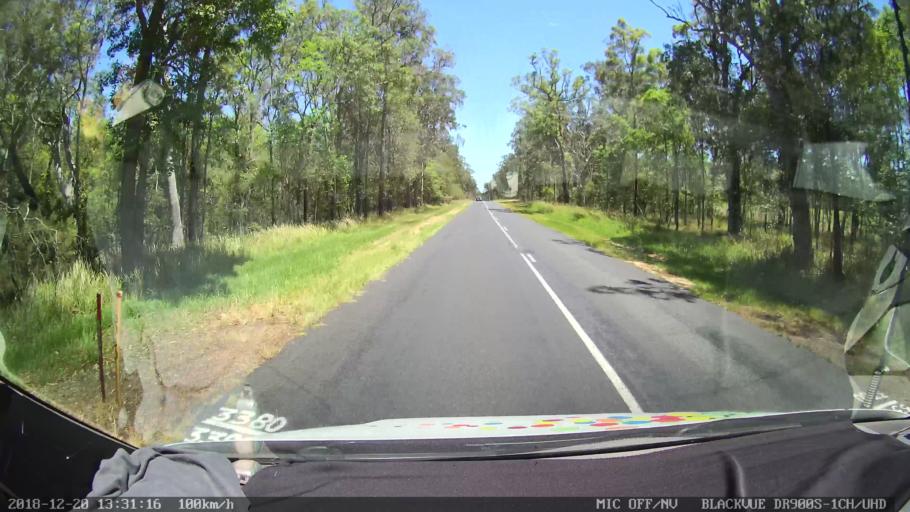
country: AU
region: New South Wales
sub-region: Clarence Valley
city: Gordon
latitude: -29.2154
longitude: 152.9896
